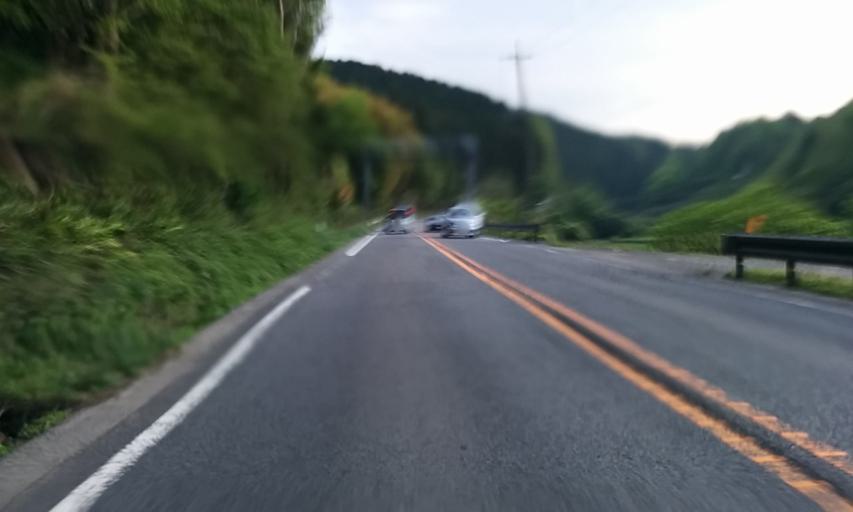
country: JP
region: Ehime
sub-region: Shikoku-chuo Shi
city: Matsuyama
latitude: 33.8020
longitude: 132.9688
